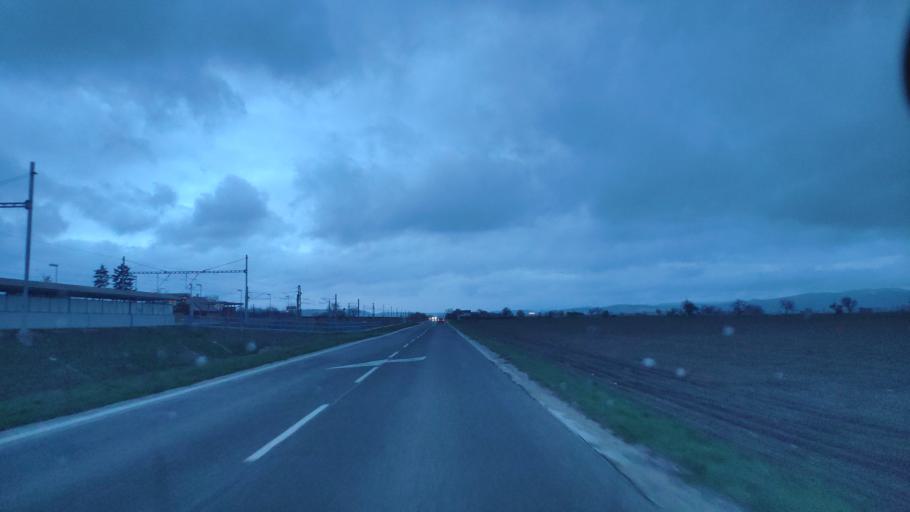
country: SK
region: Trenciansky
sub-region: Okres Nove Mesto nad Vahom
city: Nove Mesto nad Vahom
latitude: 48.8365
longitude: 17.9185
